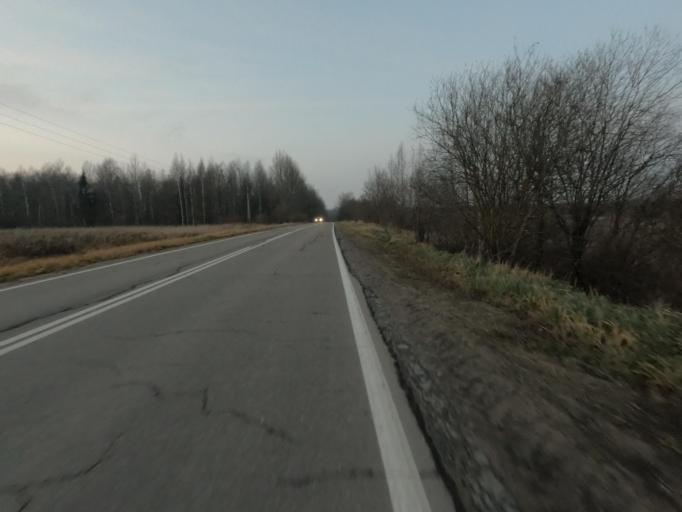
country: RU
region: Leningrad
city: Kirovsk
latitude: 59.8630
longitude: 30.9815
